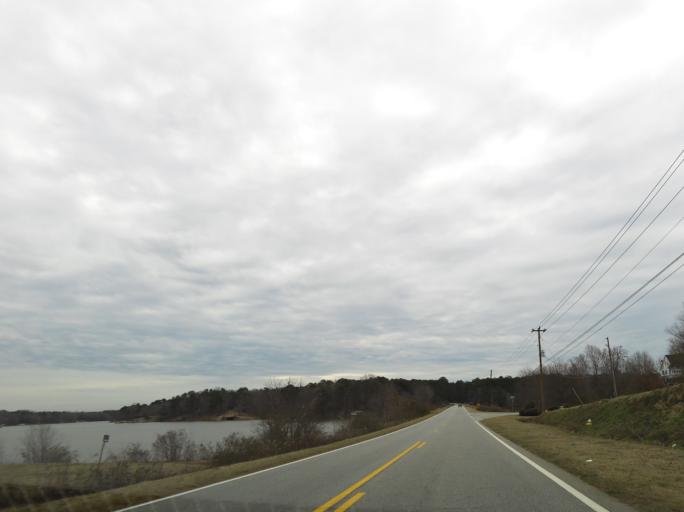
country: US
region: Georgia
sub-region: Bibb County
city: West Point
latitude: 32.8331
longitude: -83.8182
